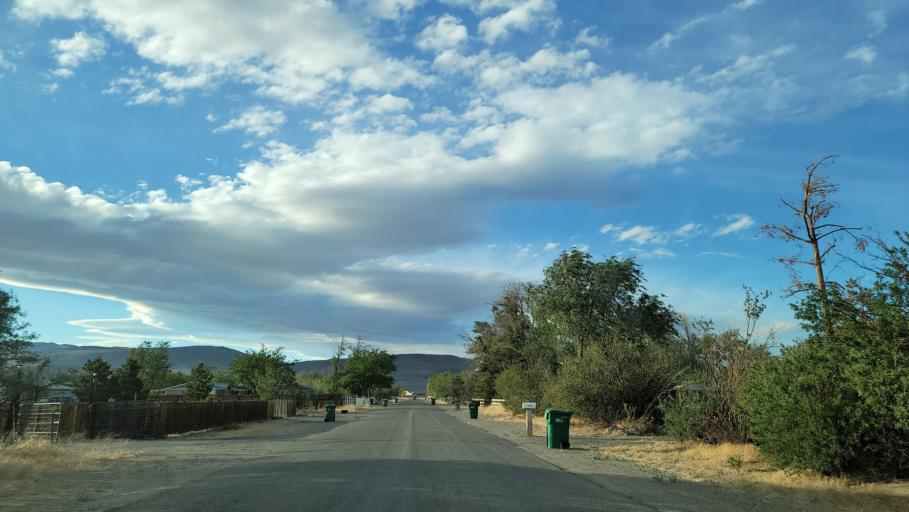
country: US
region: Nevada
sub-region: Lyon County
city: Silver Springs
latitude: 39.3955
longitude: -119.2374
